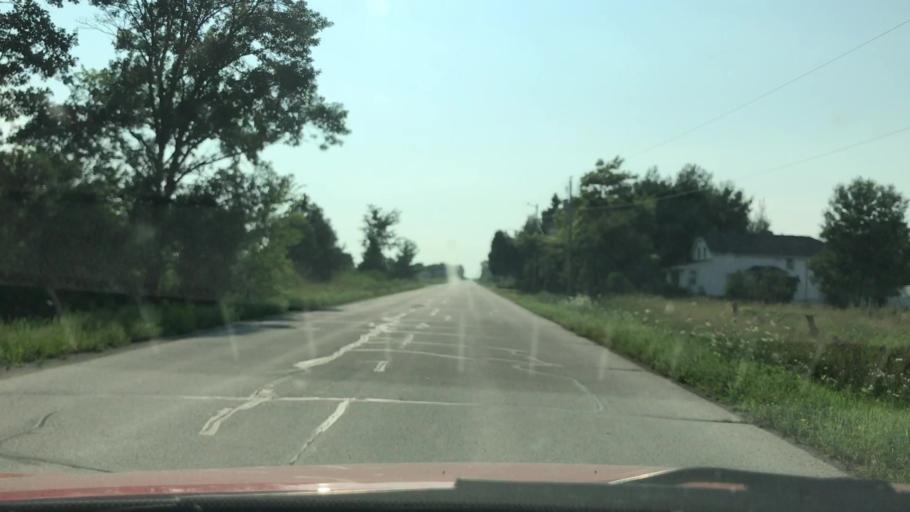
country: US
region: Wisconsin
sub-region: Brown County
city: Oneida
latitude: 44.4298
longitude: -88.1558
